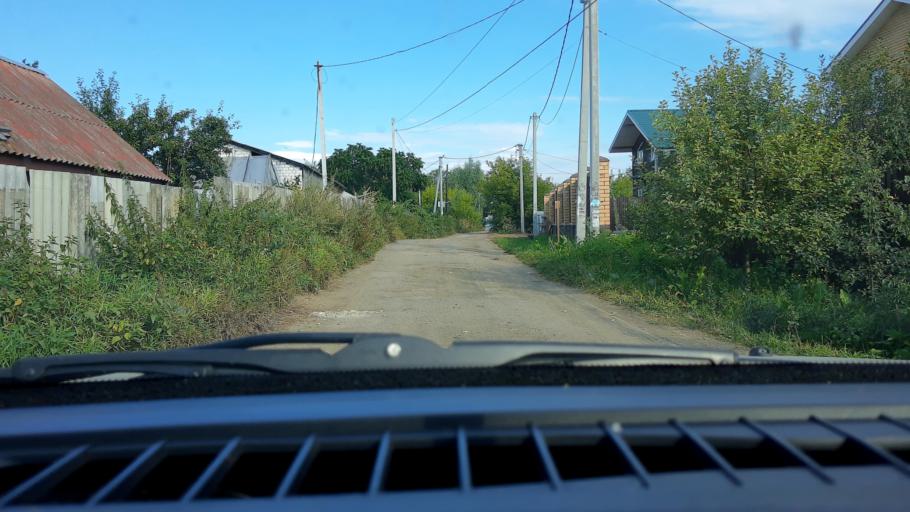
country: RU
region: Nizjnij Novgorod
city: Burevestnik
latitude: 56.1663
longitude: 43.7366
